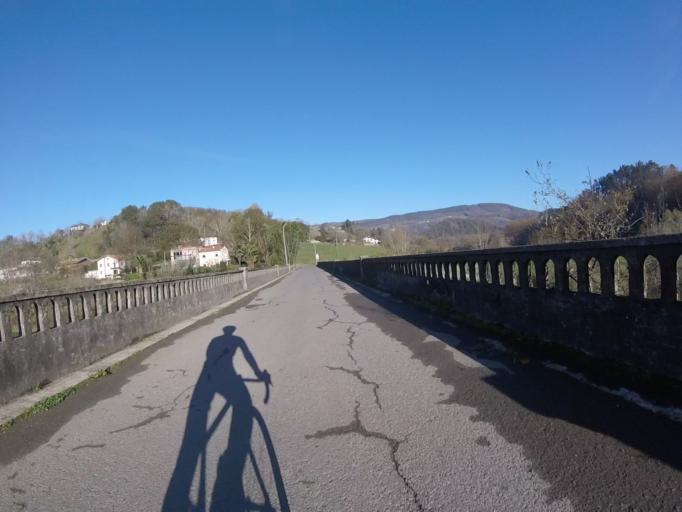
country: ES
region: Basque Country
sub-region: Provincia de Guipuzcoa
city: Usurbil
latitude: 43.2704
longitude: -2.0672
